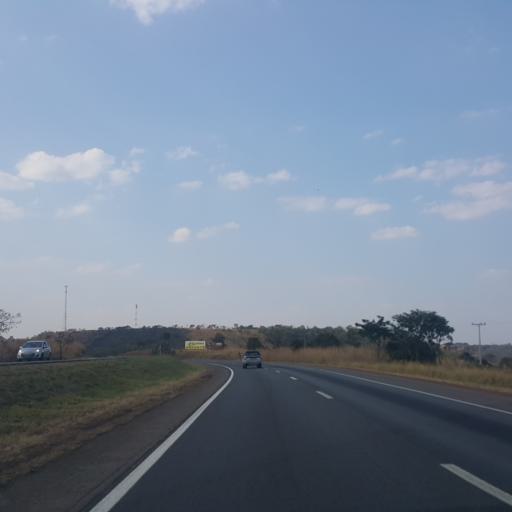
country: BR
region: Goias
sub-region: Abadiania
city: Abadiania
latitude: -16.1081
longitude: -48.5261
